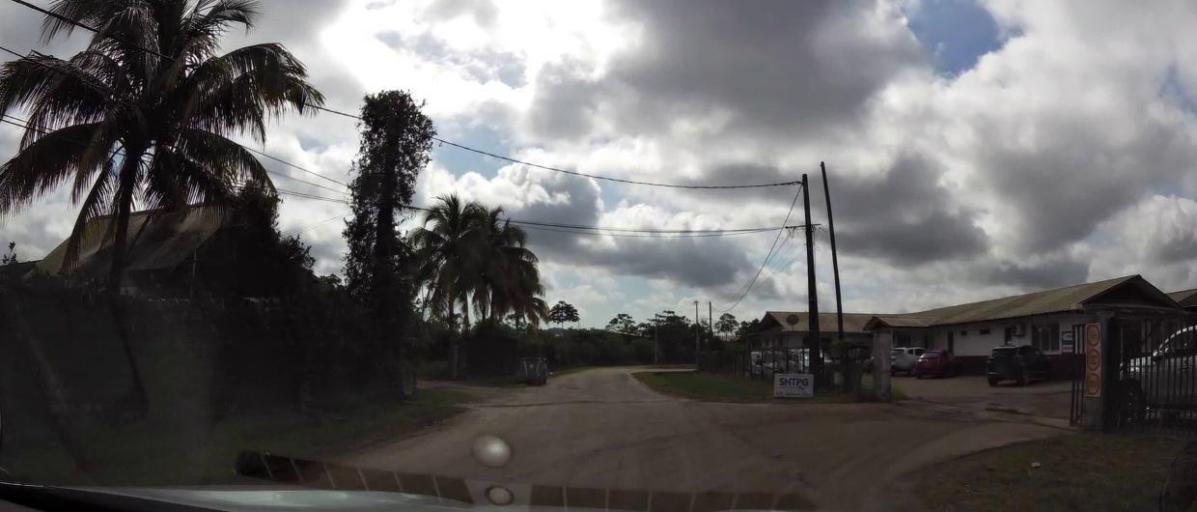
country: GF
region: Guyane
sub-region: Guyane
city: Cayenne
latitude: 4.8943
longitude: -52.3356
